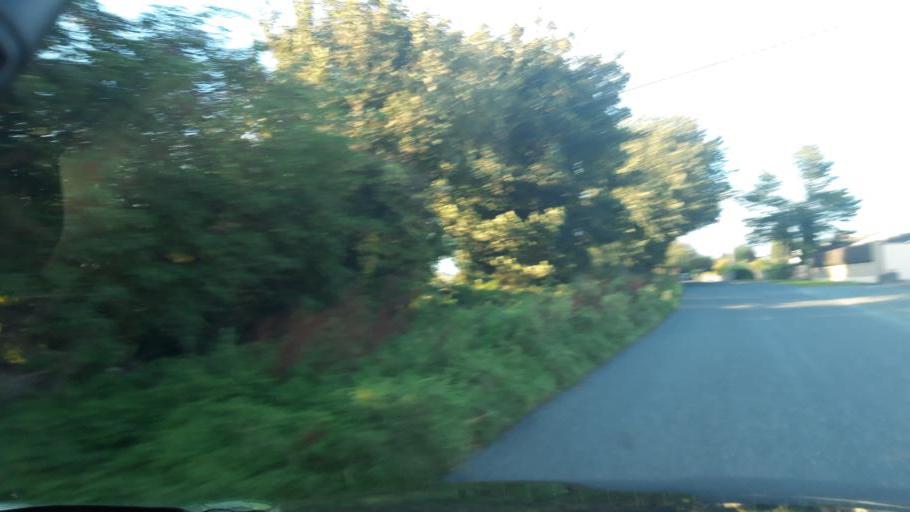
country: IE
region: Leinster
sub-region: An Iarmhi
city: Athlone
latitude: 53.4305
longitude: -7.8747
